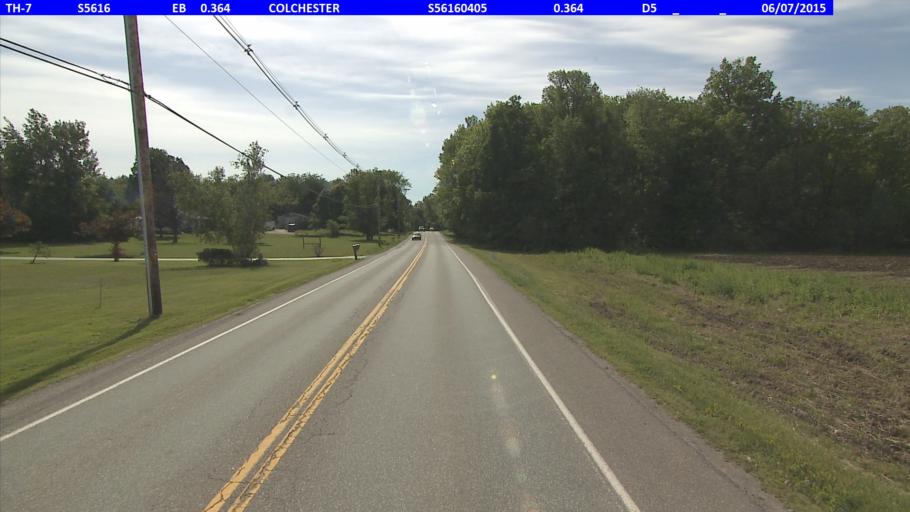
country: US
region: Vermont
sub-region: Chittenden County
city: Colchester
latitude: 44.5263
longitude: -73.1657
